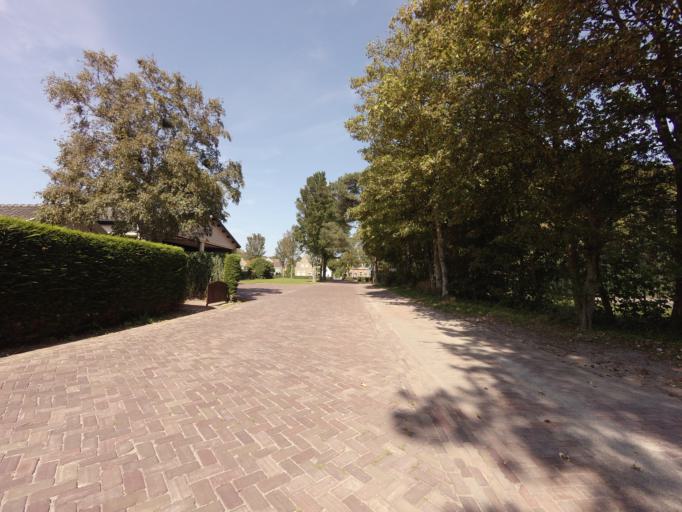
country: NL
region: Friesland
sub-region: Gemeente Schiermonnikoog
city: Schiermonnikoog
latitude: 53.4795
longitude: 6.1657
